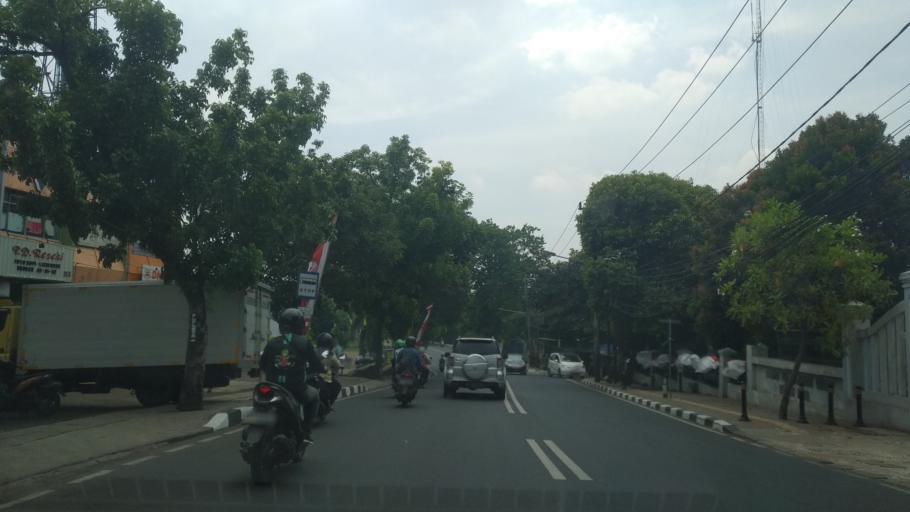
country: ID
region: Banten
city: South Tangerang
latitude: -6.2559
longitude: 106.7688
